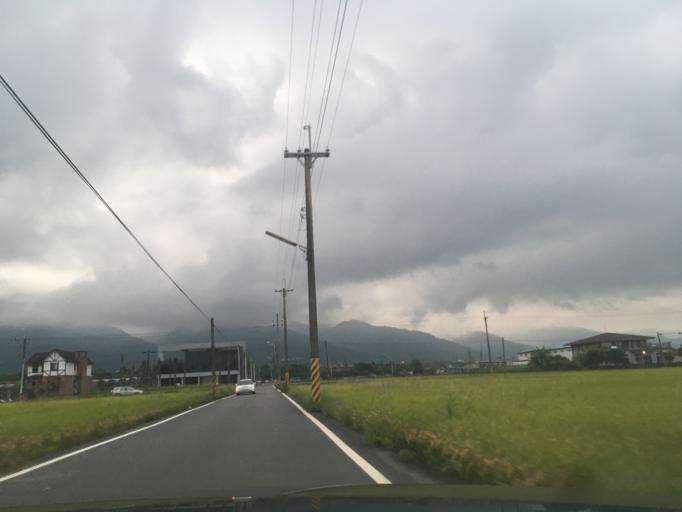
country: TW
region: Taiwan
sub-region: Yilan
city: Yilan
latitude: 24.8186
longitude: 121.7866
